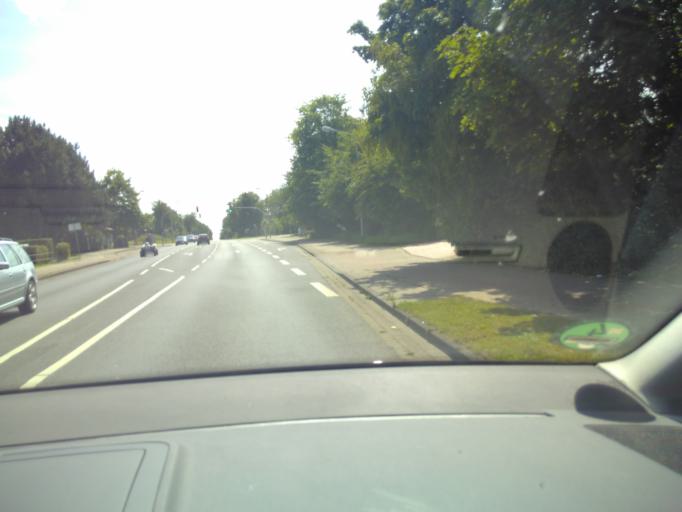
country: DE
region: Lower Saxony
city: Cuxhaven
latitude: 53.8153
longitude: 8.6628
